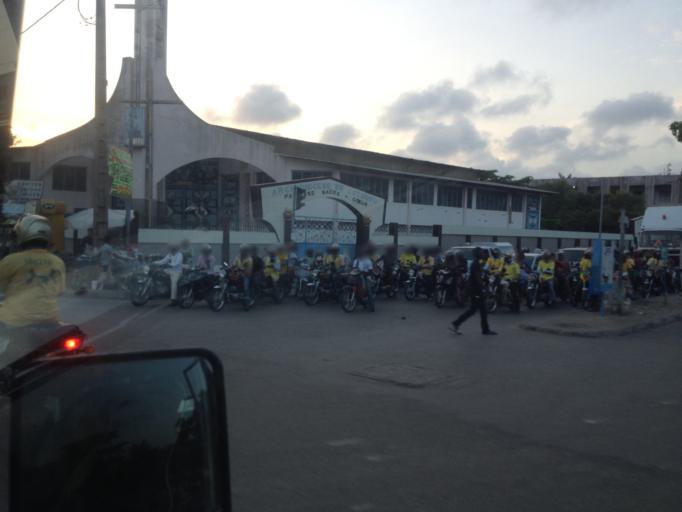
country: BJ
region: Littoral
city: Cotonou
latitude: 6.3720
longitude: 2.4469
